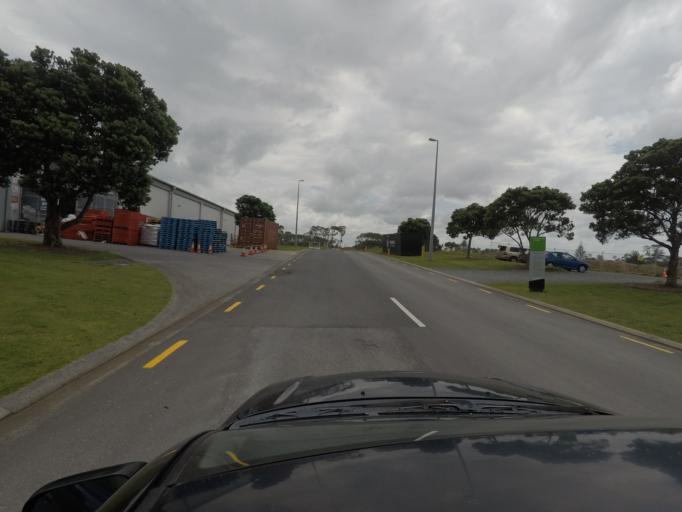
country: NZ
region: Auckland
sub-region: Auckland
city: Mangere
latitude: -36.9973
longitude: 174.7898
